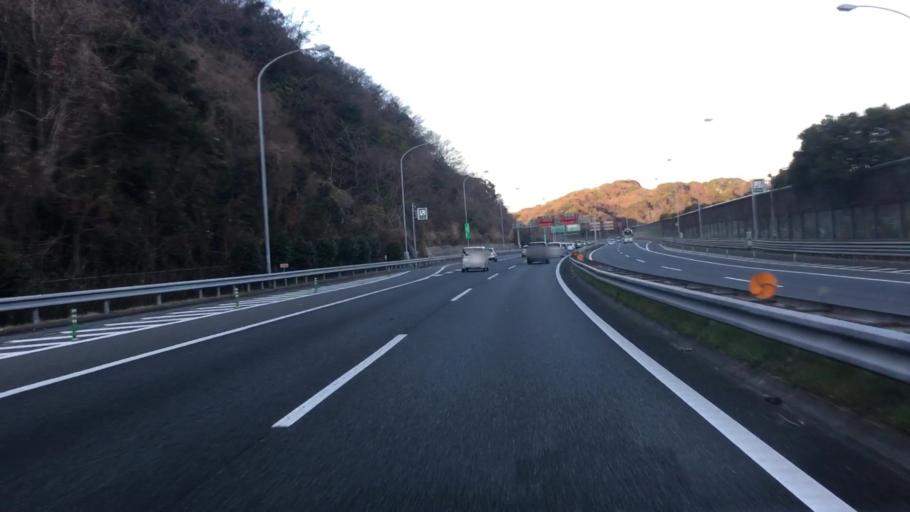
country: JP
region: Kanagawa
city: Zushi
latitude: 35.3423
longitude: 139.5911
